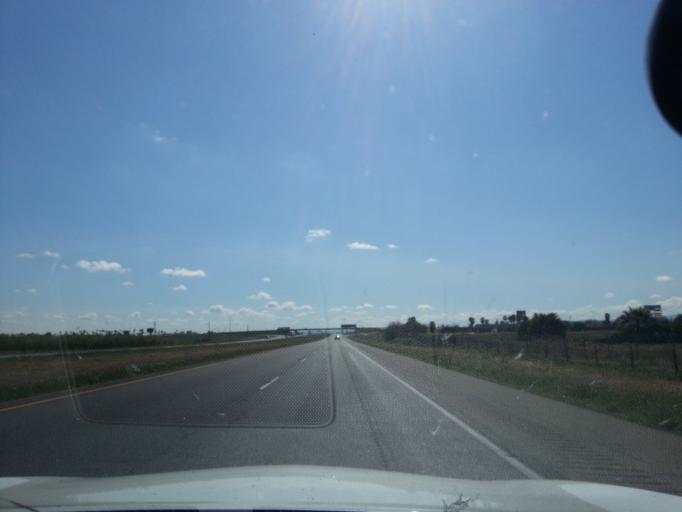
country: US
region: California
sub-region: Fresno County
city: Huron
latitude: 36.2609
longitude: -120.2484
